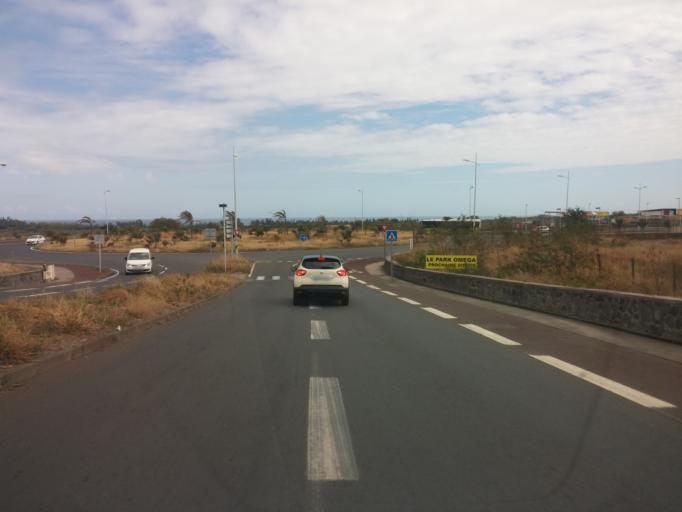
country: RE
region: Reunion
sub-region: Reunion
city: Le Port
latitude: -20.9710
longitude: 55.2970
